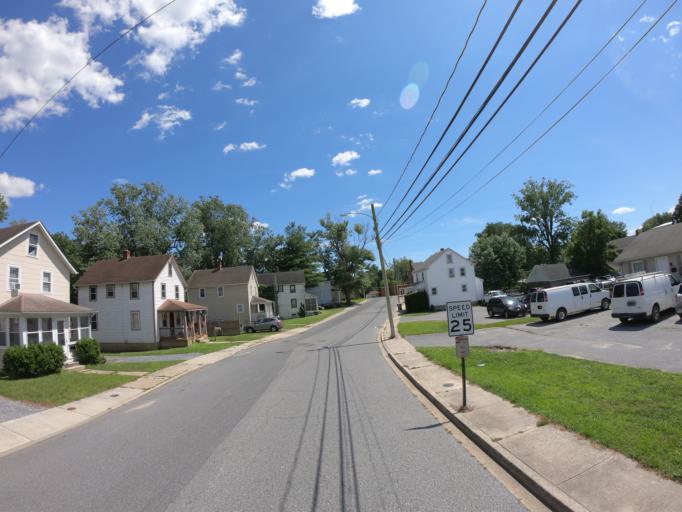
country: US
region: Delaware
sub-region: Sussex County
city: Milford
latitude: 38.9166
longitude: -75.4275
